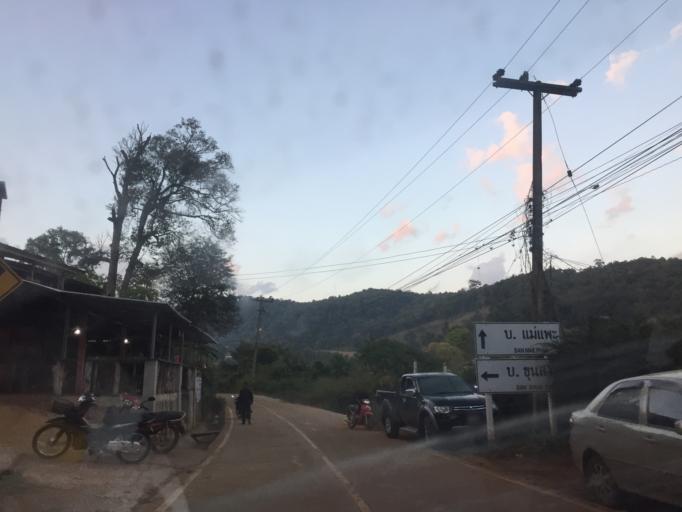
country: TH
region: Chiang Mai
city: Samoeng
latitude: 19.0061
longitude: 98.7077
